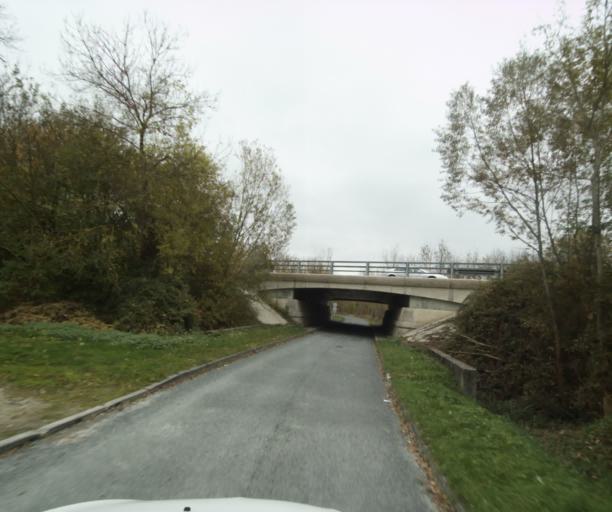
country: FR
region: Poitou-Charentes
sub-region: Departement de la Charente-Maritime
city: Les Gonds
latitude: 45.7305
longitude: -0.6243
